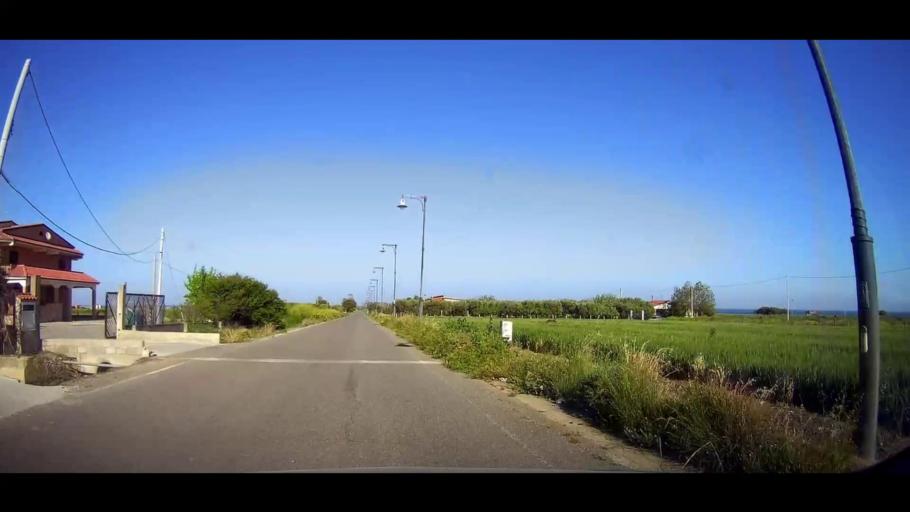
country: IT
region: Calabria
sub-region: Provincia di Crotone
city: Crotone
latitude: 39.0248
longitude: 17.1755
